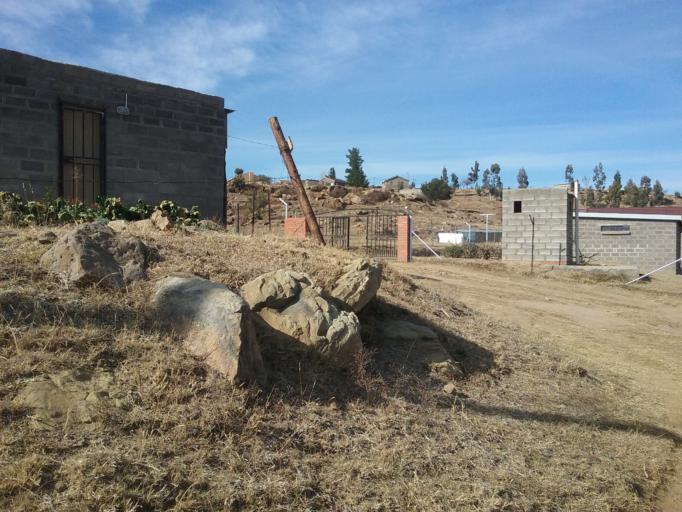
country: LS
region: Maseru
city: Maseru
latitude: -29.4180
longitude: 27.5503
